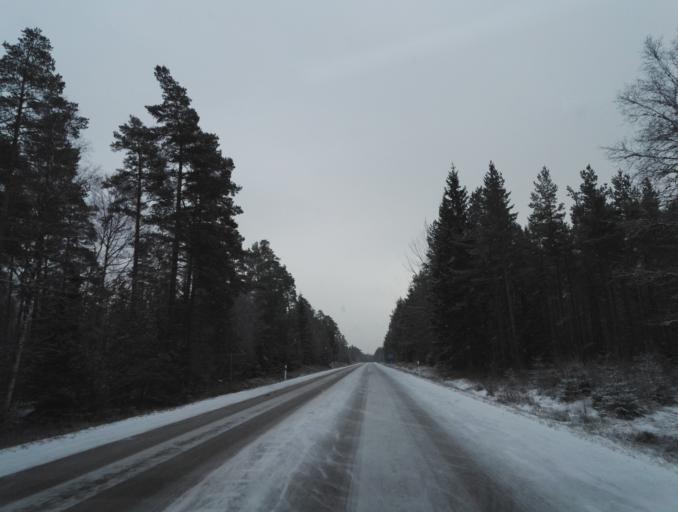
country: SE
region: Kronoberg
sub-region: Uppvidinge Kommun
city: Lenhovda
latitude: 56.9842
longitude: 15.2942
